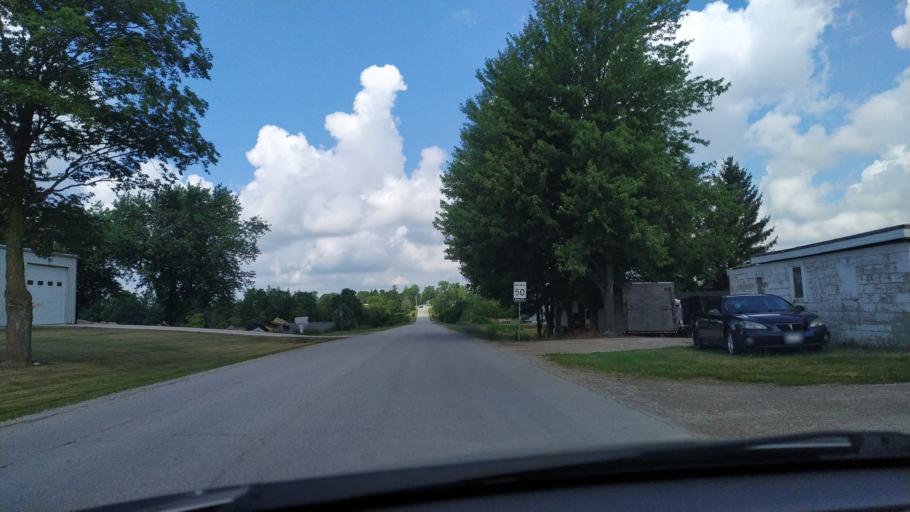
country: CA
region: Ontario
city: Huron East
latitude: 43.4580
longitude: -81.1992
